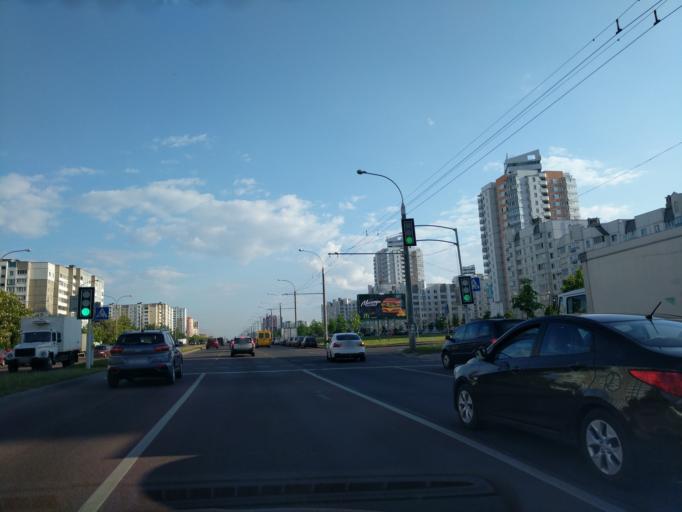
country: BY
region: Minsk
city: Zhdanovichy
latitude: 53.9146
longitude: 27.4366
